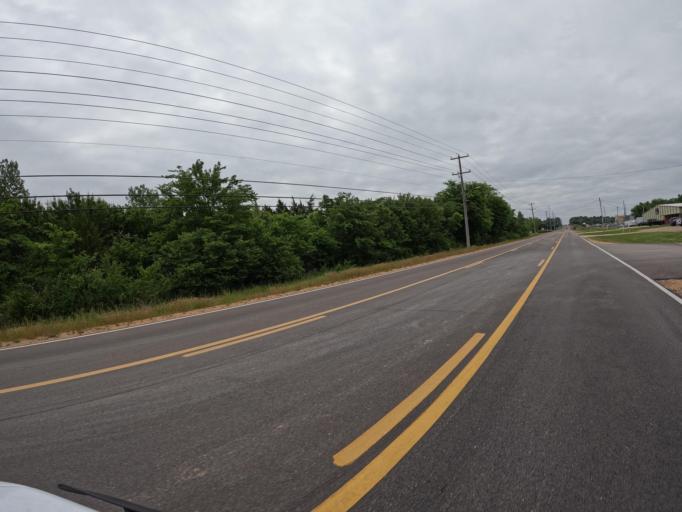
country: US
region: Mississippi
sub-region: Lee County
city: Tupelo
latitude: 34.2769
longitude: -88.7643
